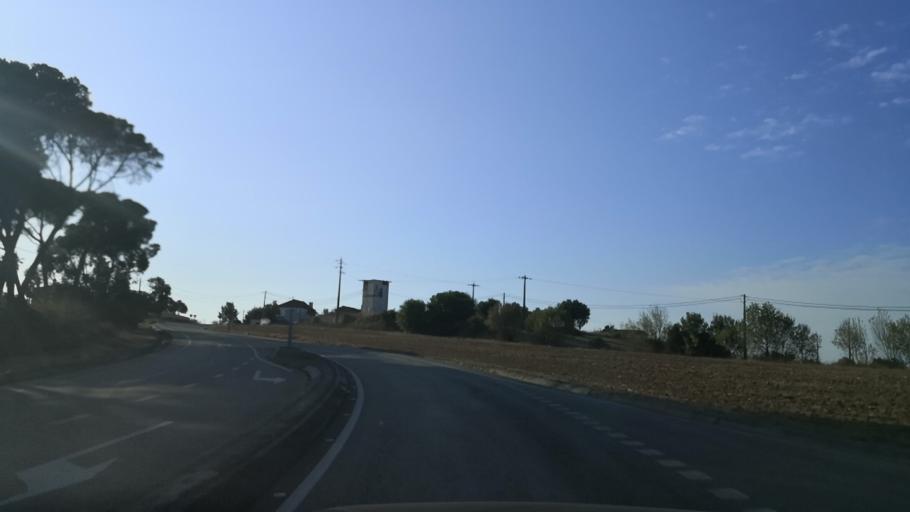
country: PT
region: Santarem
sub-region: Alcanena
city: Alcanena
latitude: 39.3465
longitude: -8.6615
